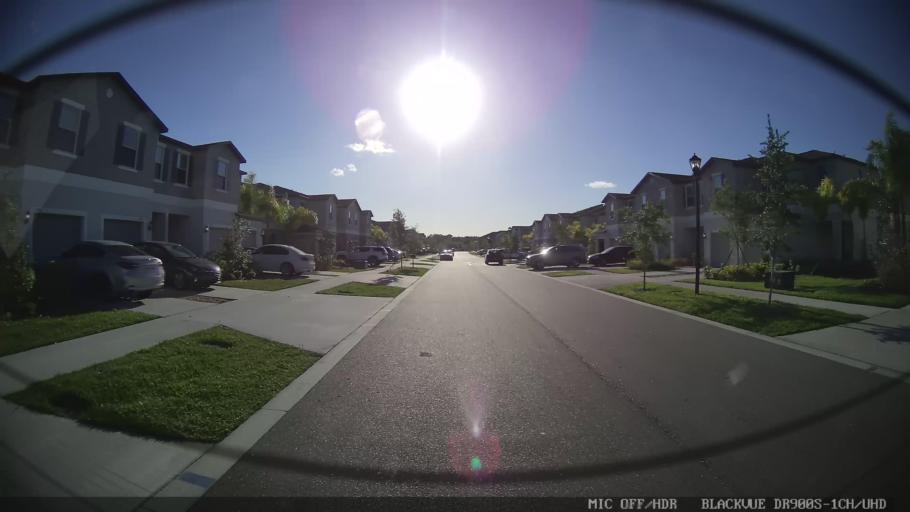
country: US
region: Florida
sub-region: Hillsborough County
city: Sun City Center
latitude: 27.7435
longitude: -82.3486
